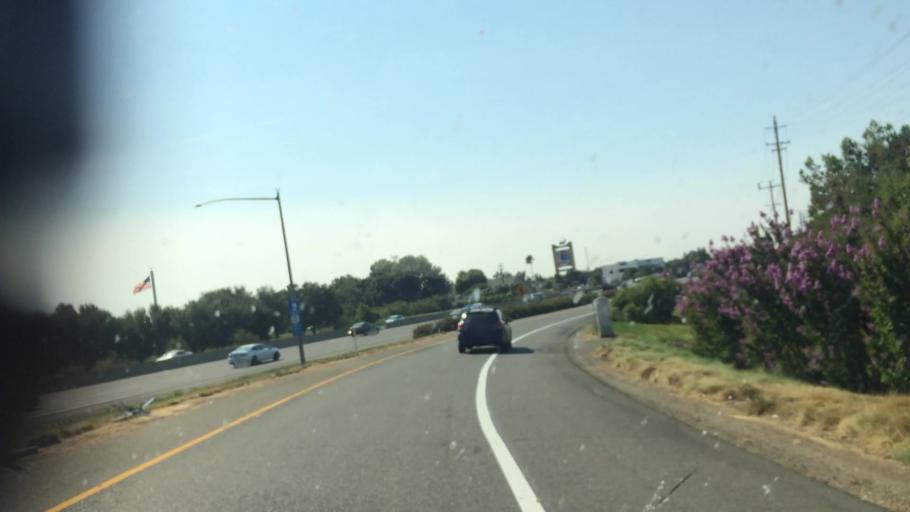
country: US
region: California
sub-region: Sacramento County
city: Elk Grove
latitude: 38.4227
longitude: -121.3956
